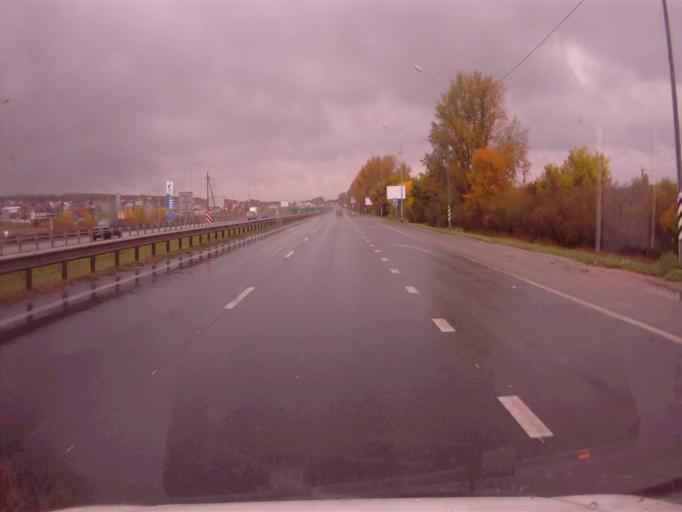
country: RU
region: Chelyabinsk
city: Dolgoderevenskoye
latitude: 55.2765
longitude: 61.3438
